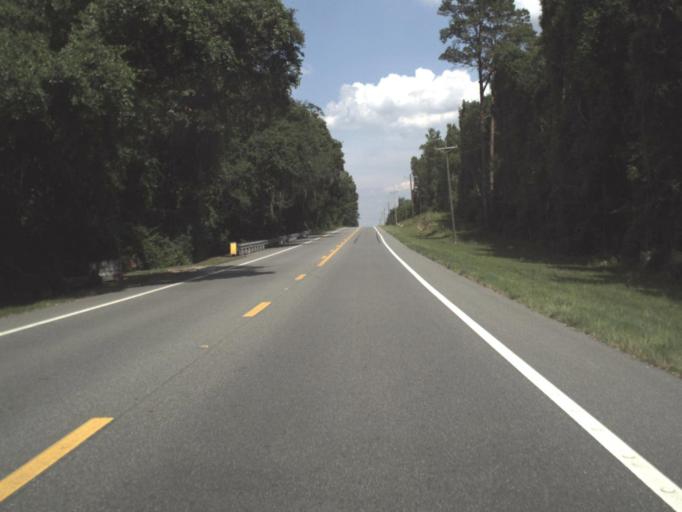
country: US
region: Florida
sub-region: Putnam County
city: Interlachen
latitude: 29.7307
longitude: -81.8605
